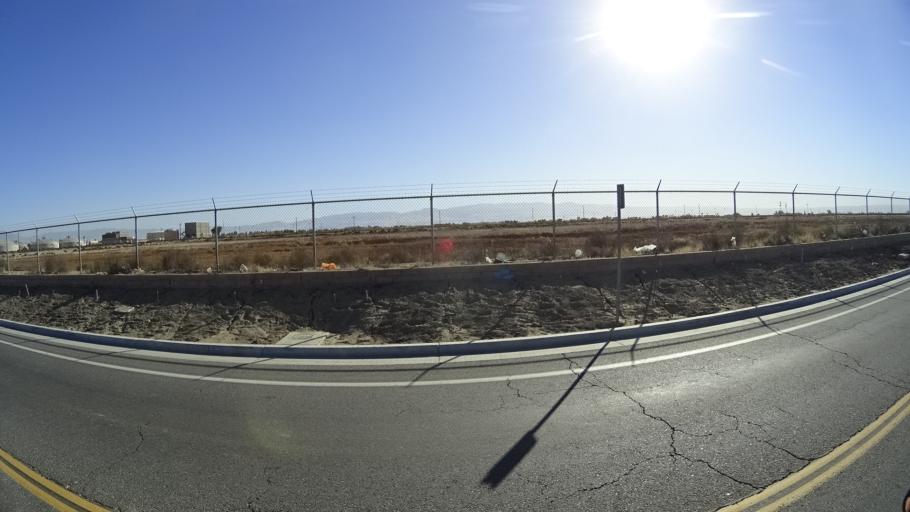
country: US
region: California
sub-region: Kern County
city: Greenfield
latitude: 35.2815
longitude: -119.0824
